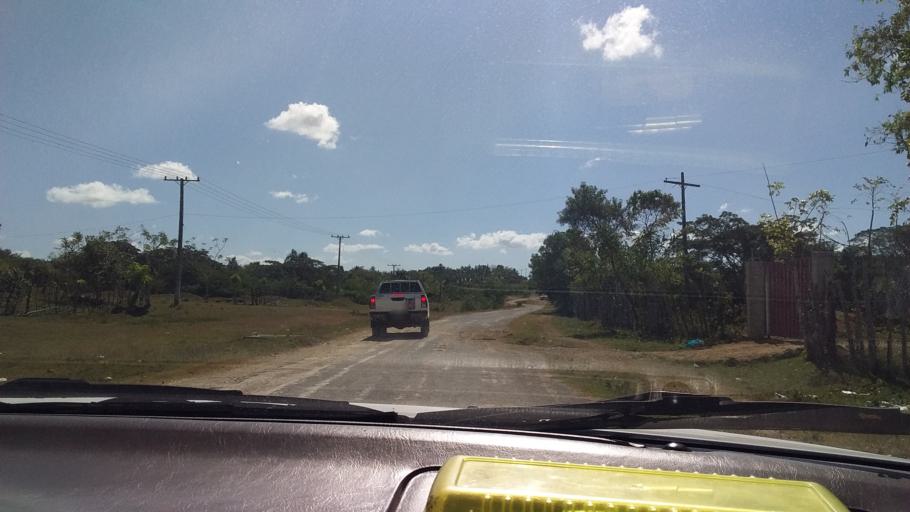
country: DO
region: Santo Domingo
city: Guerra
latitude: 18.5679
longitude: -69.7833
